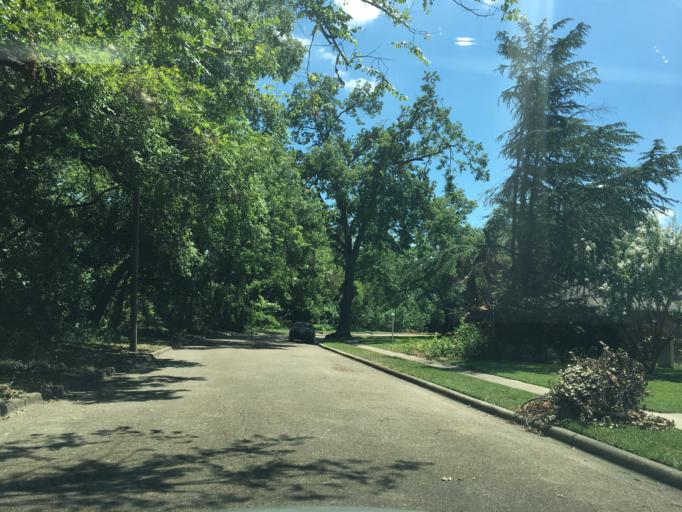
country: US
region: Texas
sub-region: Dallas County
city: Garland
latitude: 32.8497
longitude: -96.7005
